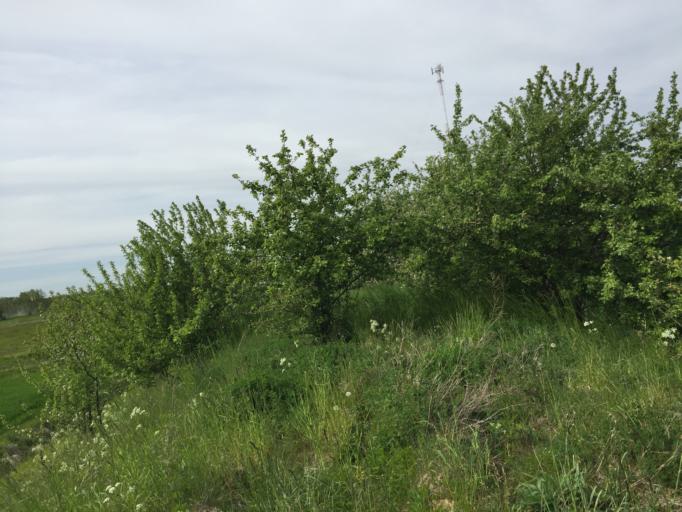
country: LT
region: Panevezys
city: Pasvalys
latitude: 56.0242
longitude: 24.1854
